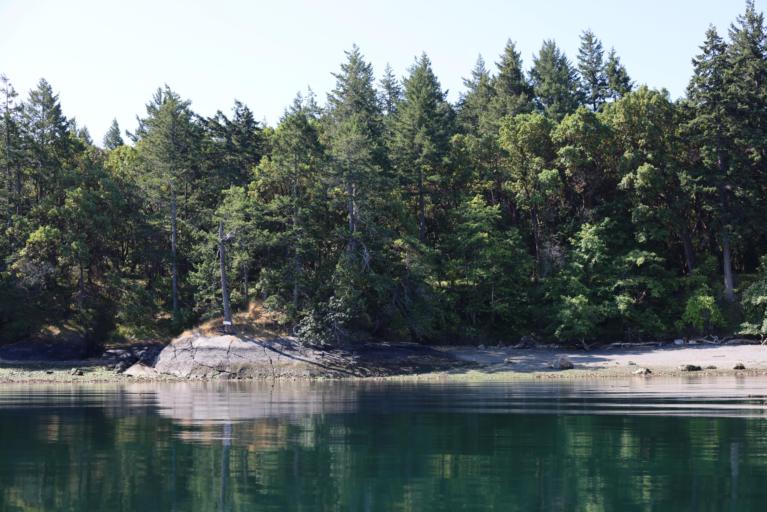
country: CA
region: British Columbia
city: Colwood
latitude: 48.3902
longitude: -123.4818
